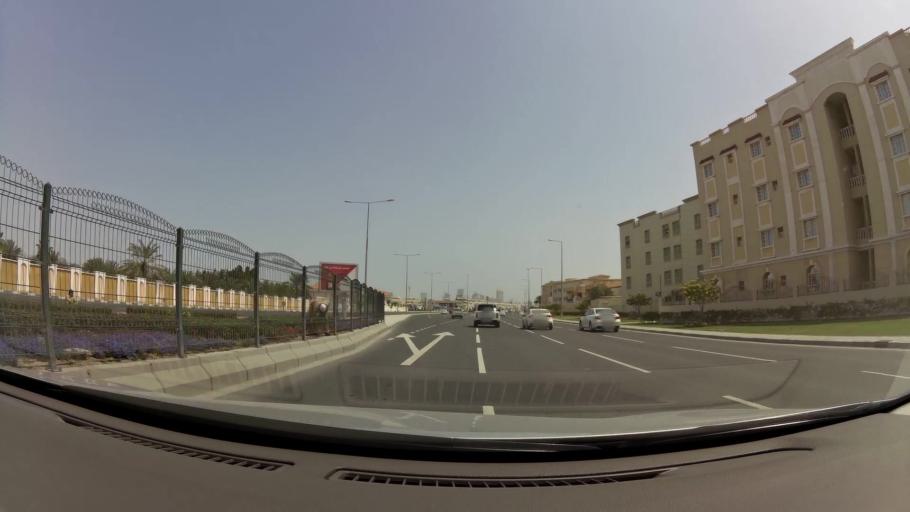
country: QA
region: Baladiyat ad Dawhah
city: Doha
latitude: 25.3226
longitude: 51.4834
